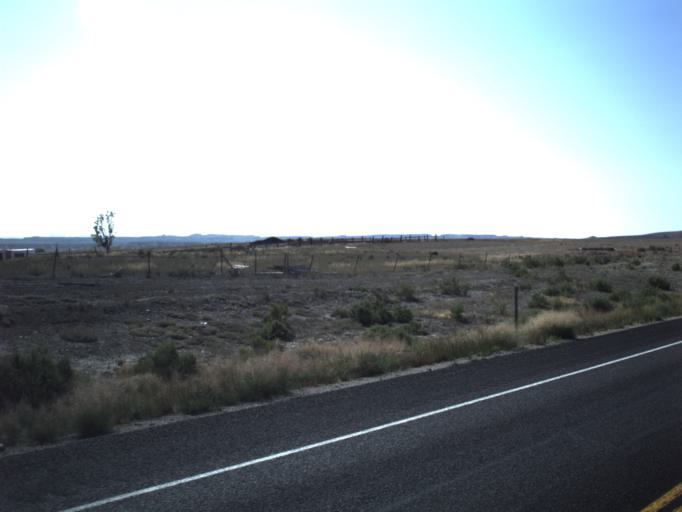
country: US
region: Utah
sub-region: Emery County
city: Ferron
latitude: 39.0662
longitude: -111.1315
